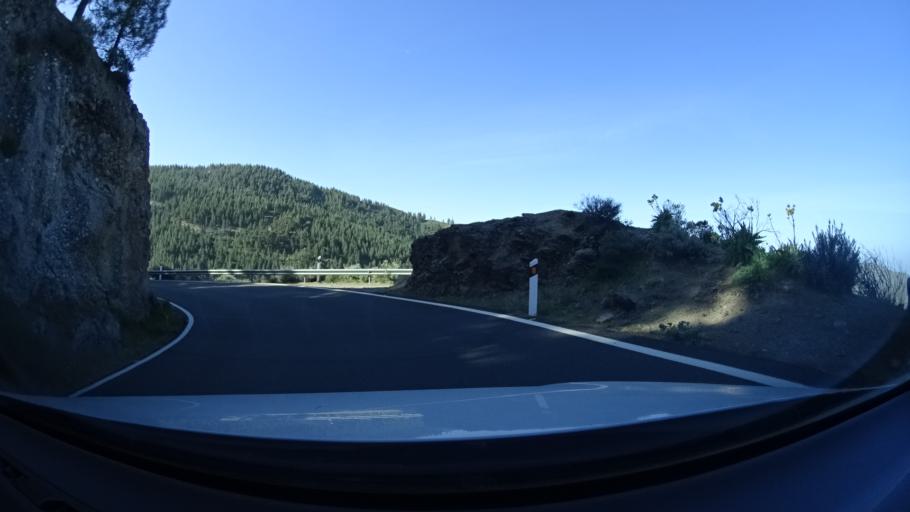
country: ES
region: Canary Islands
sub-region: Provincia de Las Palmas
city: Artenara
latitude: 28.0273
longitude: -15.6241
